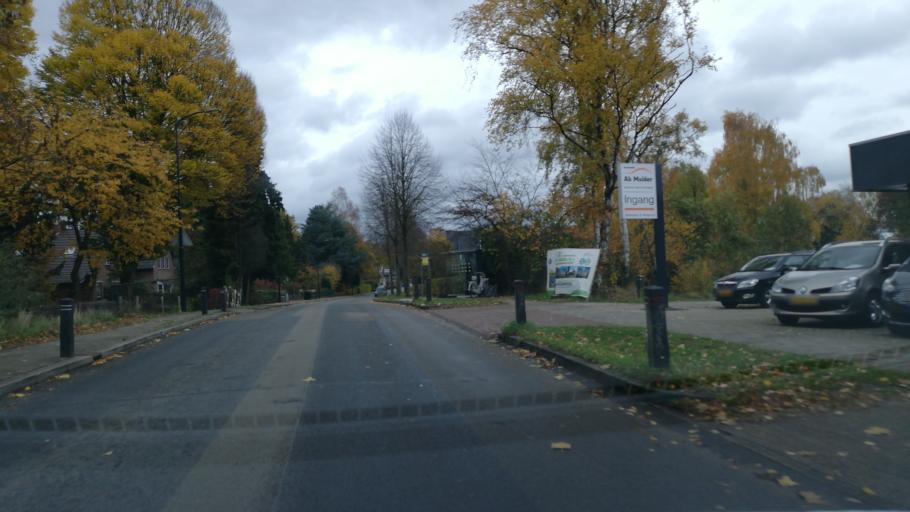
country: NL
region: Gelderland
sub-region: Gemeente Apeldoorn
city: Beekbergen
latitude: 52.1848
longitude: 5.9357
